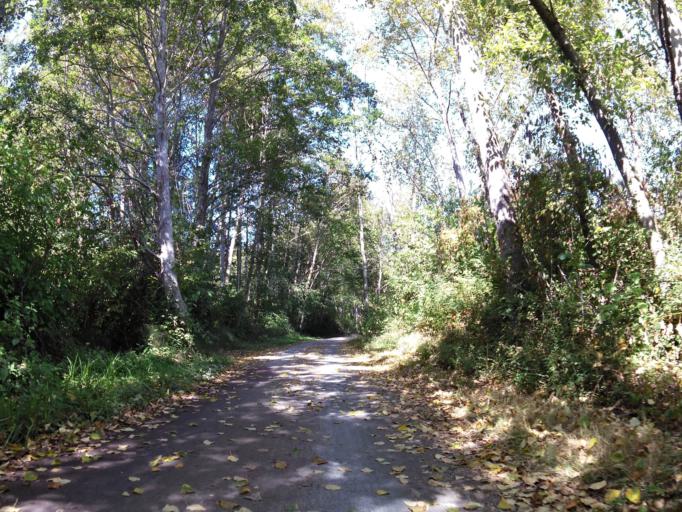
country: CA
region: British Columbia
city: Victoria
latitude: 48.5451
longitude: -123.3846
